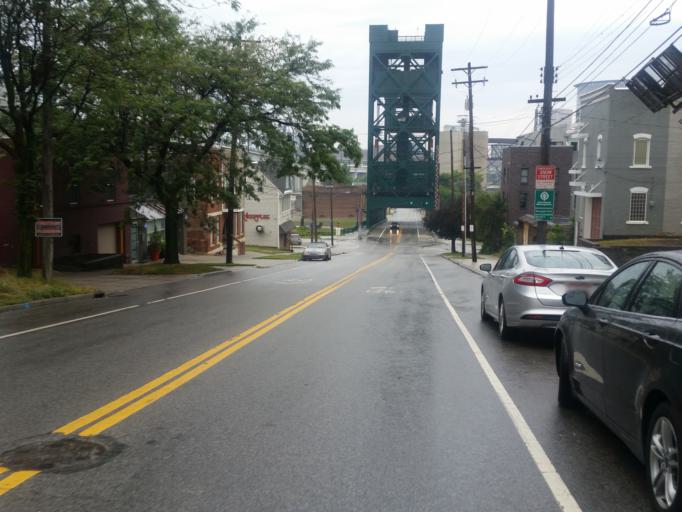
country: US
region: Ohio
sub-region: Cuyahoga County
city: Cleveland
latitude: 41.4865
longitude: -81.7004
